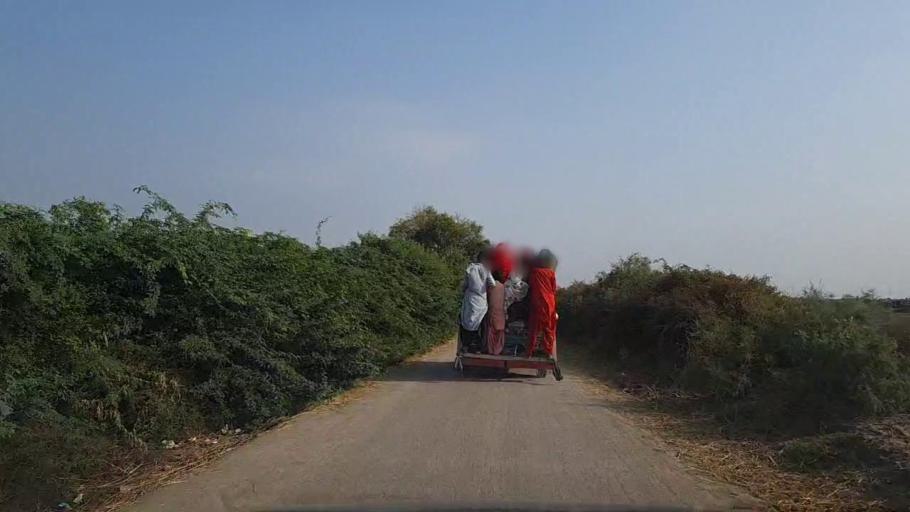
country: PK
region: Sindh
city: Thatta
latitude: 24.6472
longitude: 67.9288
